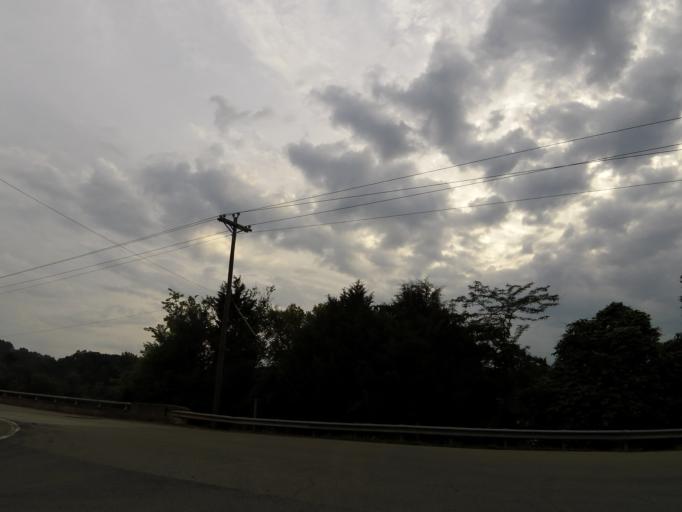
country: US
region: Tennessee
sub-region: Loudon County
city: Greenback
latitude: 35.6405
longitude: -84.2159
